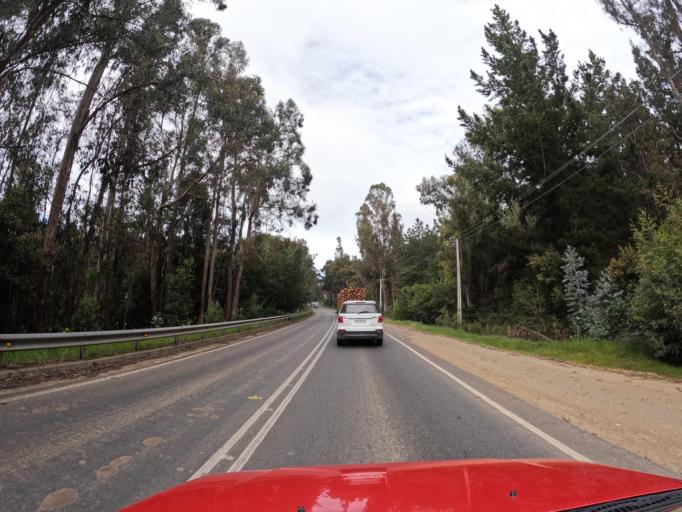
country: CL
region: O'Higgins
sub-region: Provincia de Colchagua
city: Santa Cruz
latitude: -34.3589
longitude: -71.8876
